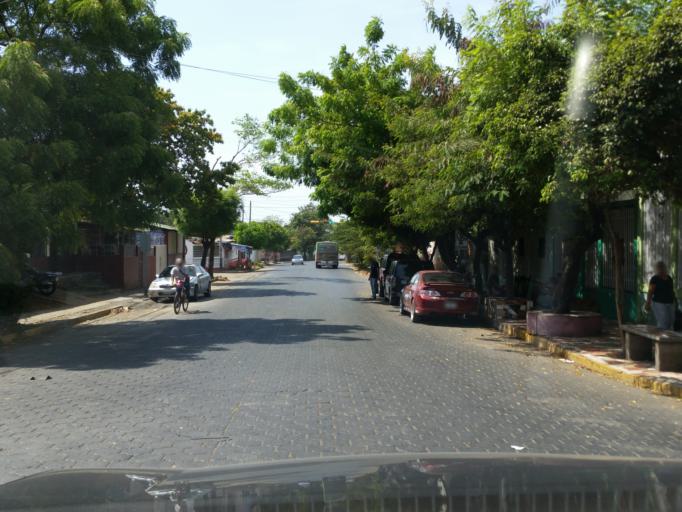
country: NI
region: Managua
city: Managua
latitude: 12.1267
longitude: -86.2512
